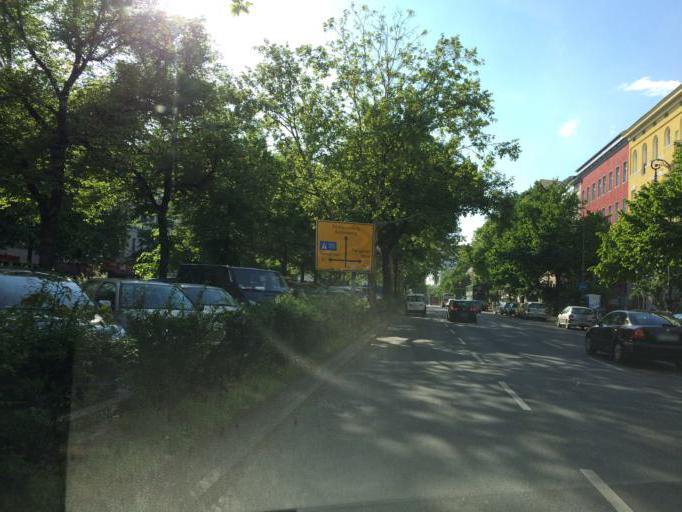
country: DE
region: Berlin
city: Bezirk Kreuzberg
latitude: 52.4925
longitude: 13.3903
